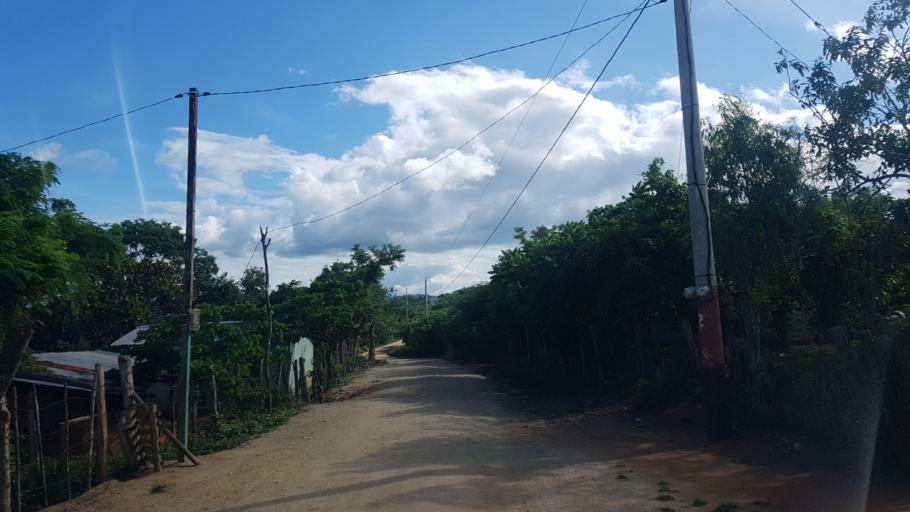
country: NI
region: Nueva Segovia
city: Mozonte
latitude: 13.6497
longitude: -86.3987
